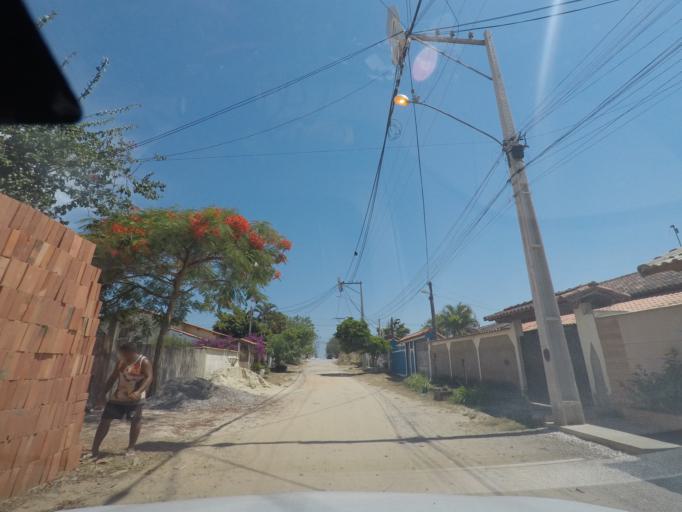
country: BR
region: Rio de Janeiro
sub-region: Marica
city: Marica
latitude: -22.9637
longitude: -42.9558
